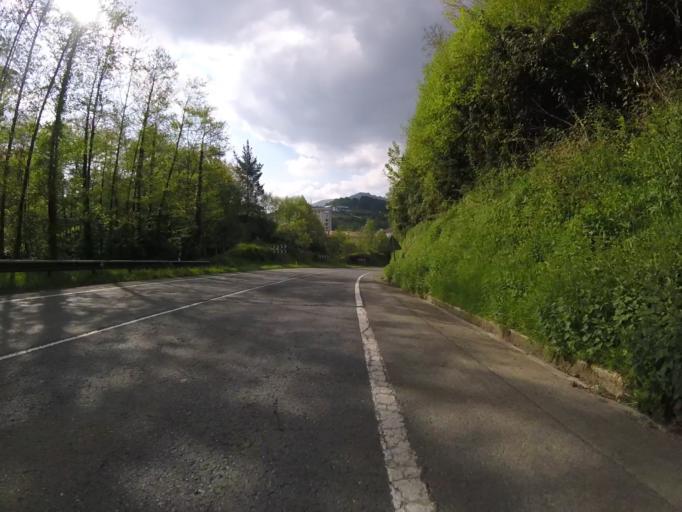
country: ES
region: Basque Country
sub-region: Provincia de Guipuzcoa
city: Azkoitia
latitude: 43.1775
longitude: -2.3171
